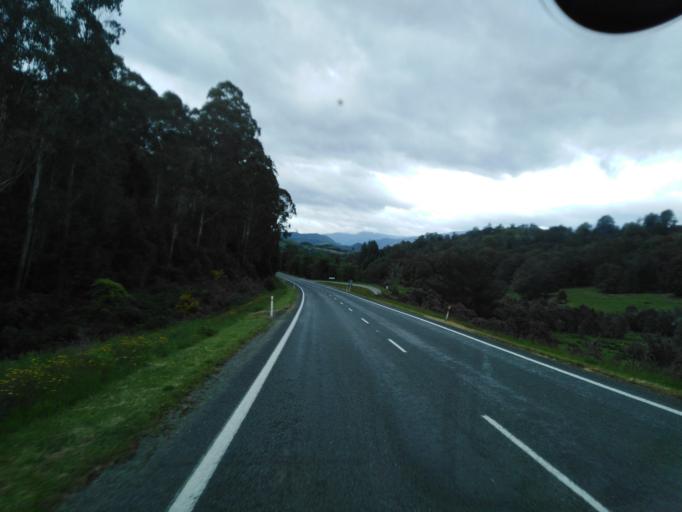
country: NZ
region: Tasman
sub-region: Tasman District
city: Wakefield
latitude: -41.6305
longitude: 172.6958
